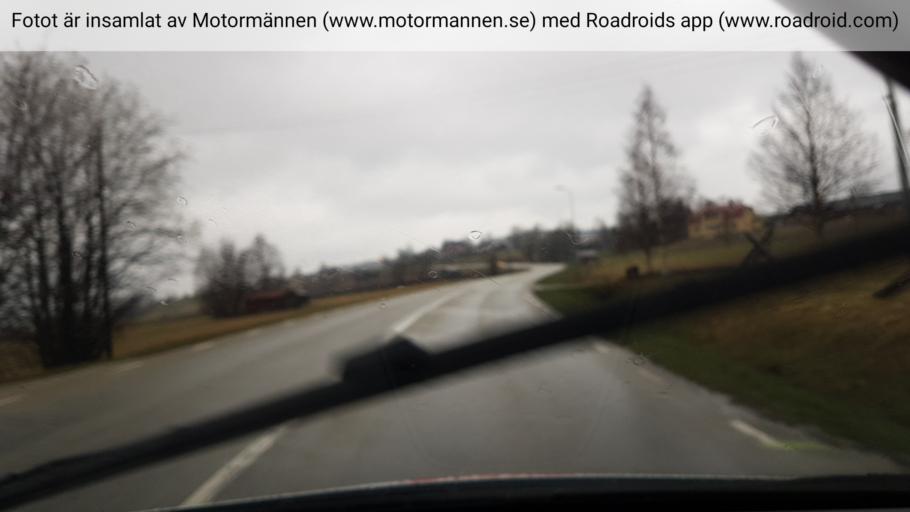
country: SE
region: Jaemtland
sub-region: Bergs Kommun
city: Hoverberg
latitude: 62.5212
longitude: 14.1935
